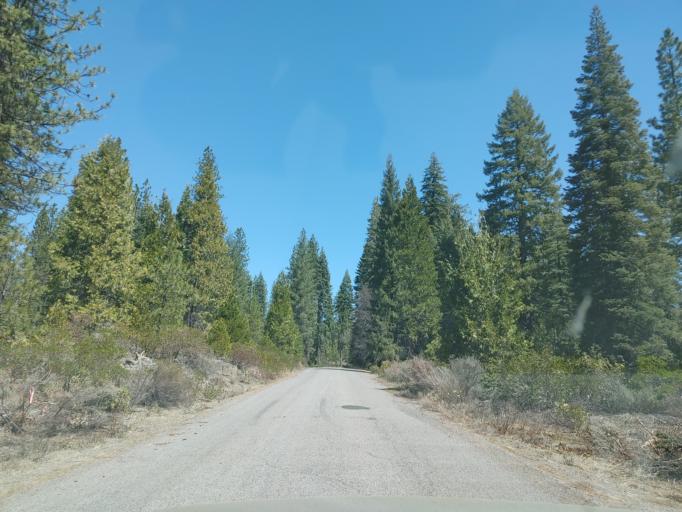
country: US
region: California
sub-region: Siskiyou County
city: McCloud
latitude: 41.2428
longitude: -121.9709
